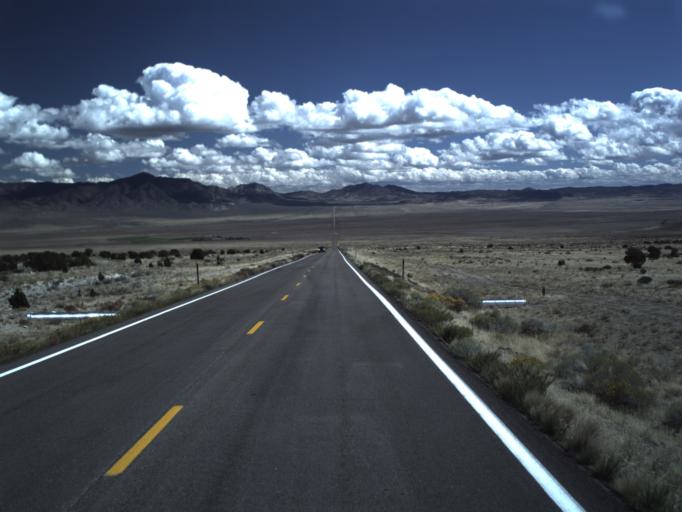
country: US
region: Utah
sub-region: Beaver County
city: Milford
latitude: 38.5021
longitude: -113.5044
